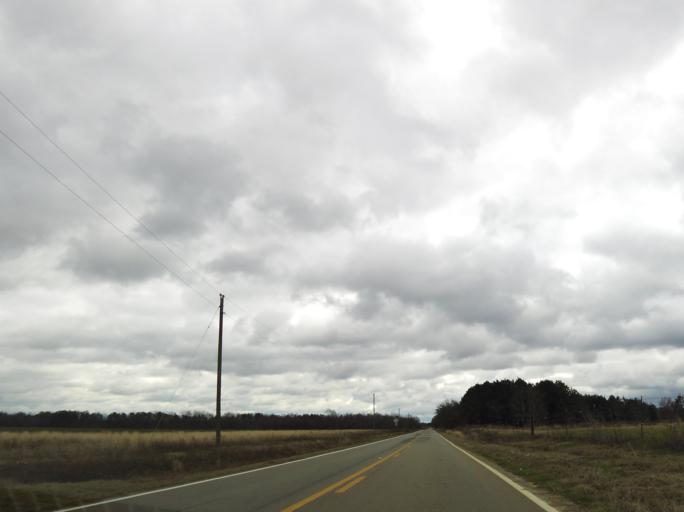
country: US
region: Georgia
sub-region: Bleckley County
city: Cochran
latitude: 32.5363
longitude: -83.3723
